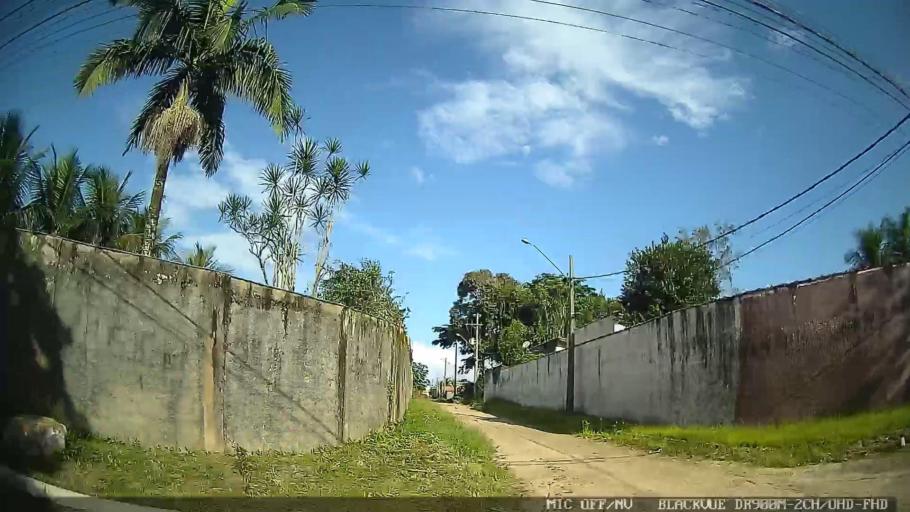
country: BR
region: Sao Paulo
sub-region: Itanhaem
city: Itanhaem
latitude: -24.1756
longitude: -46.8234
